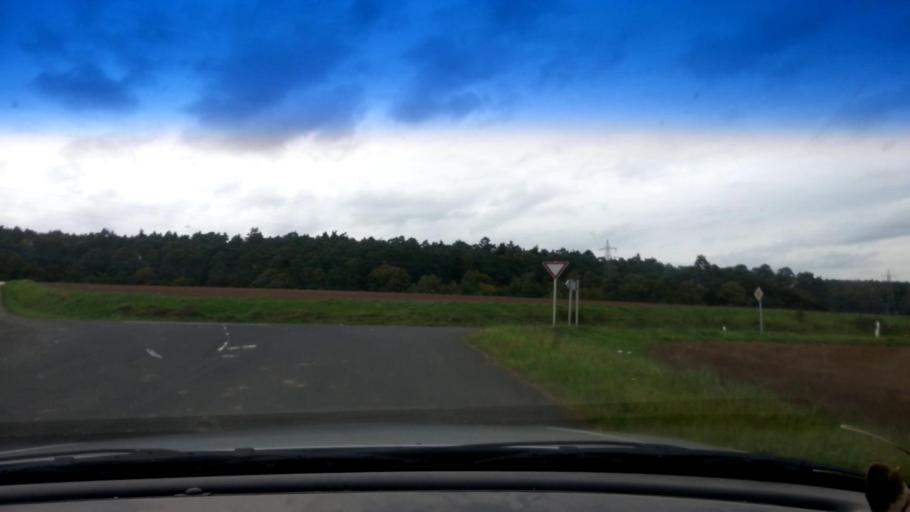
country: DE
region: Bavaria
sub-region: Upper Franconia
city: Gerach
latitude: 50.0360
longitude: 10.7673
